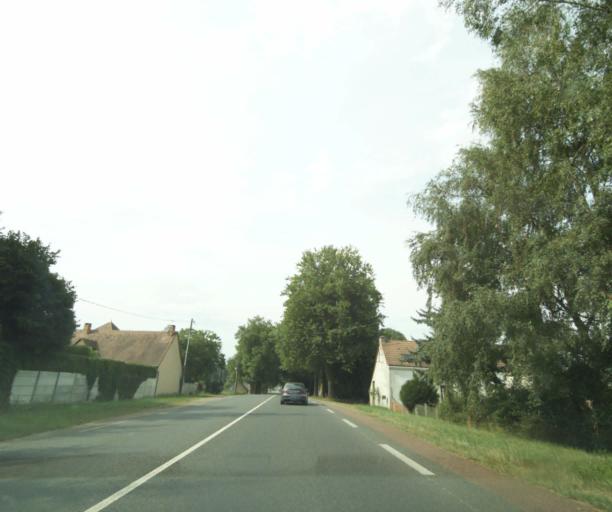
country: FR
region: Pays de la Loire
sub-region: Departement de la Sarthe
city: Mulsanne
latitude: 47.8985
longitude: 0.2452
